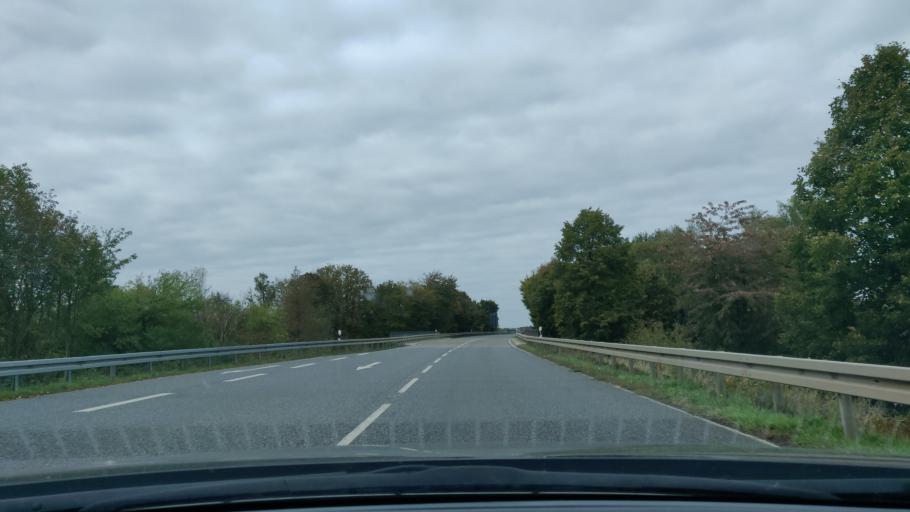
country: DE
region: Hesse
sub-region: Regierungsbezirk Kassel
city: Wabern
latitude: 51.1003
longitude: 9.3591
